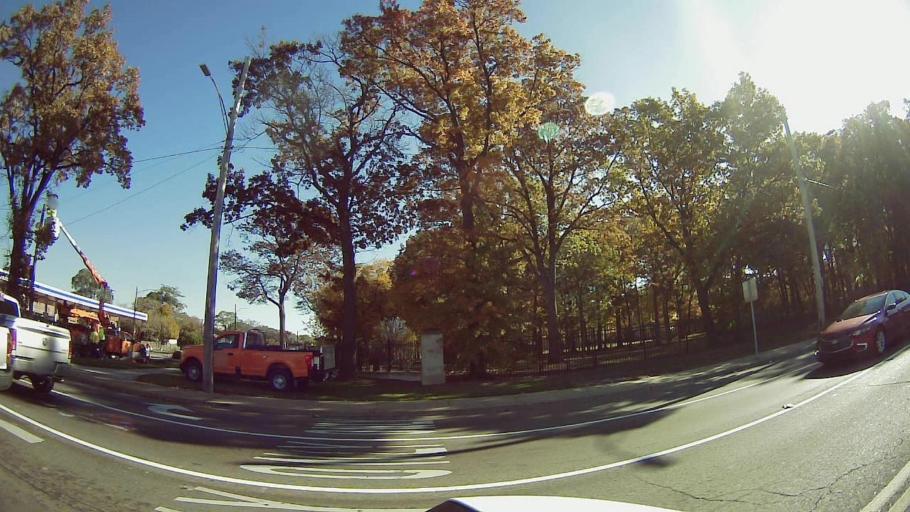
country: US
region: Michigan
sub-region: Oakland County
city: Oak Park
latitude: 42.4177
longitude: -83.1604
